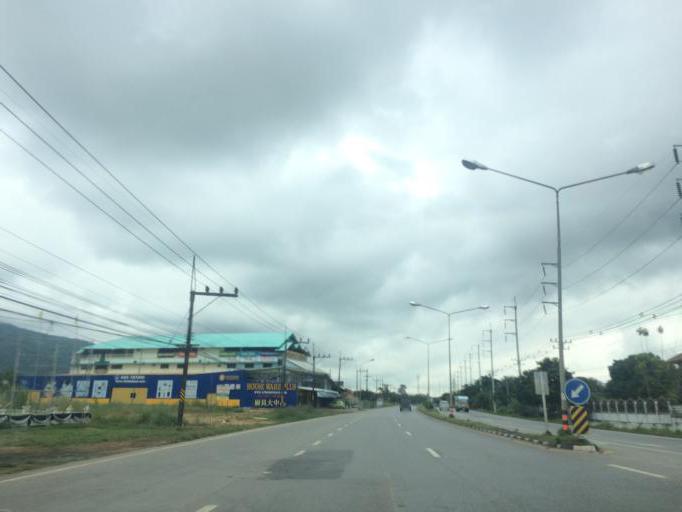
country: TH
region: Chiang Rai
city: Mae Chan
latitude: 20.0849
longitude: 99.8746
